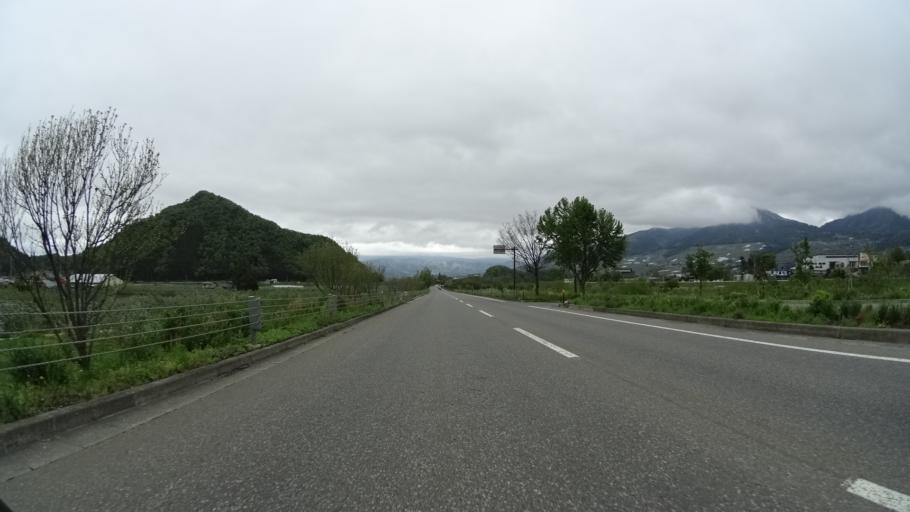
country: JP
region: Nagano
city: Nakano
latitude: 36.7472
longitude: 138.4017
